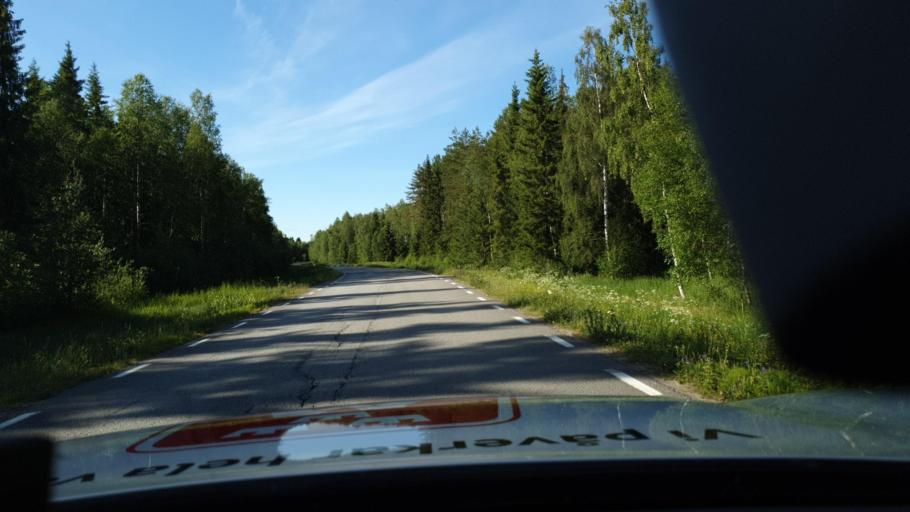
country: SE
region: Norrbotten
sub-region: Kalix Kommun
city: Toere
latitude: 65.8519
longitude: 22.6797
